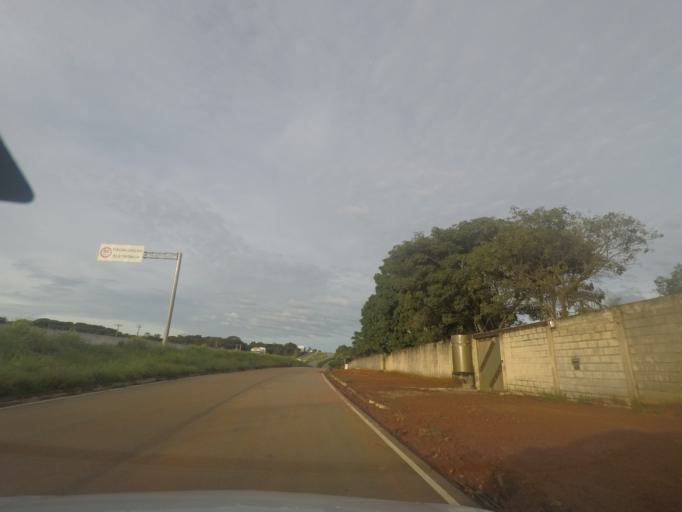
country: BR
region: Goias
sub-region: Trindade
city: Trindade
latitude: -16.7341
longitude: -49.4012
